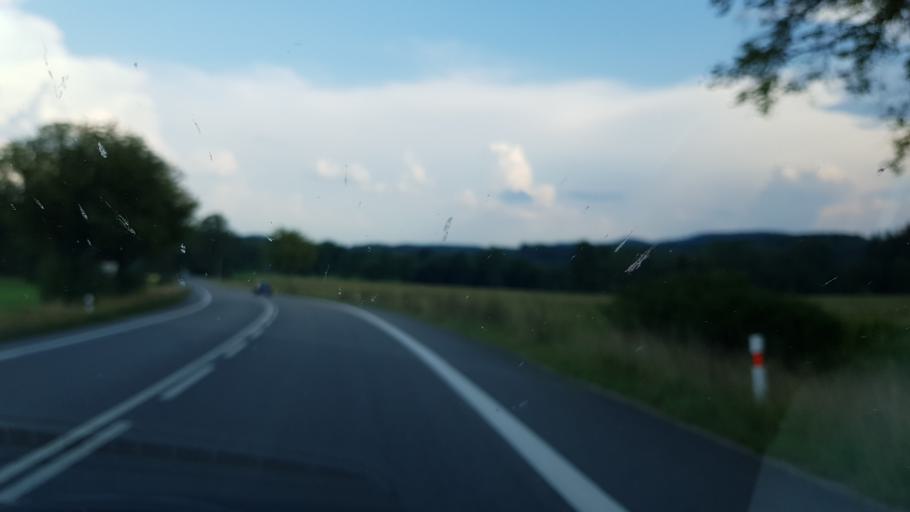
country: CZ
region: Pardubicky
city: Zamberk
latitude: 50.0993
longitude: 16.4045
